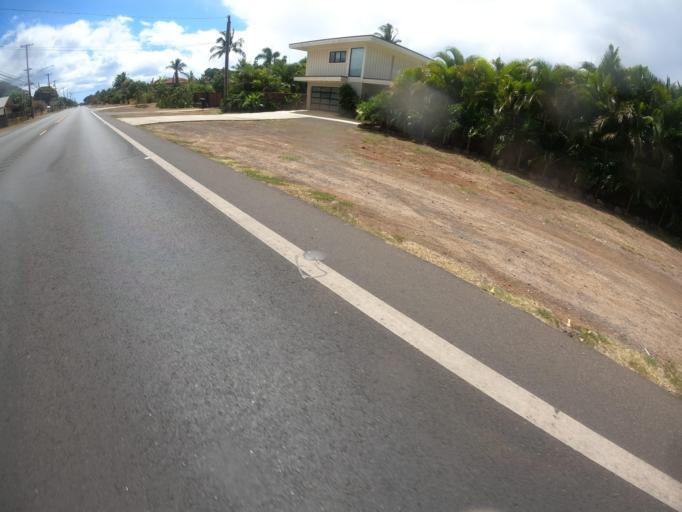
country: US
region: Hawaii
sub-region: Honolulu County
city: Makaha
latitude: 21.4749
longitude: -158.2187
